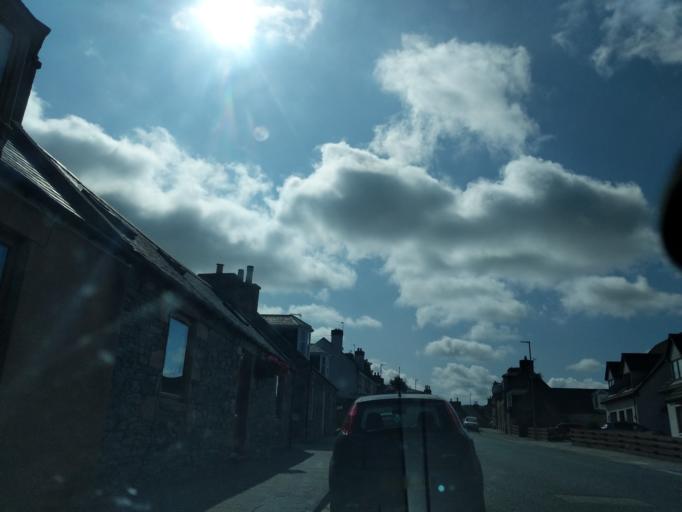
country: GB
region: Scotland
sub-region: Moray
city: Dufftown
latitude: 57.4487
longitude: -3.1300
